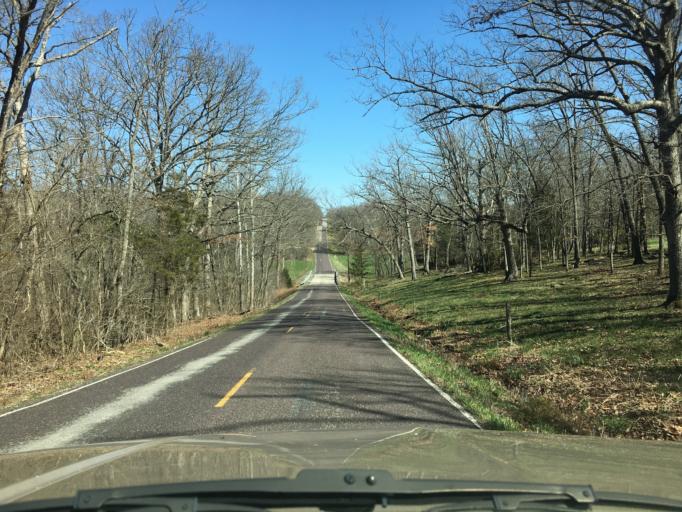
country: US
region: Missouri
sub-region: Franklin County
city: New Haven
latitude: 38.5458
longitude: -91.3302
